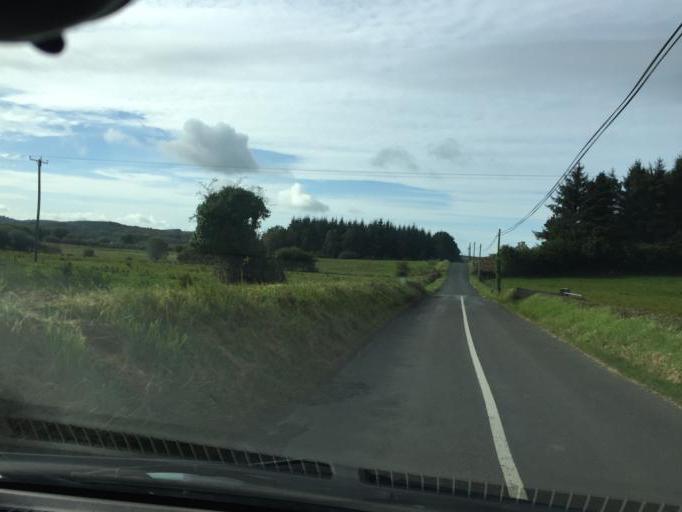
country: IE
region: Connaught
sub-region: Roscommon
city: Boyle
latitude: 54.0701
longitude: -8.2154
